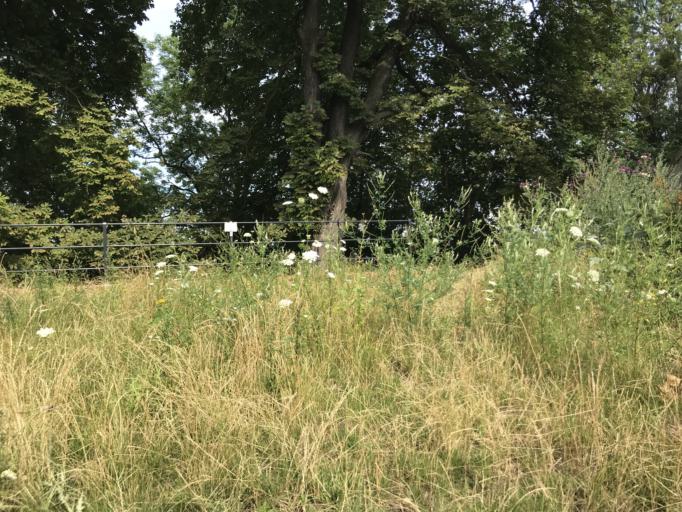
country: PL
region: Pomeranian Voivodeship
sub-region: Gdansk
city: Gdansk
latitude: 54.3446
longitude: 18.6420
